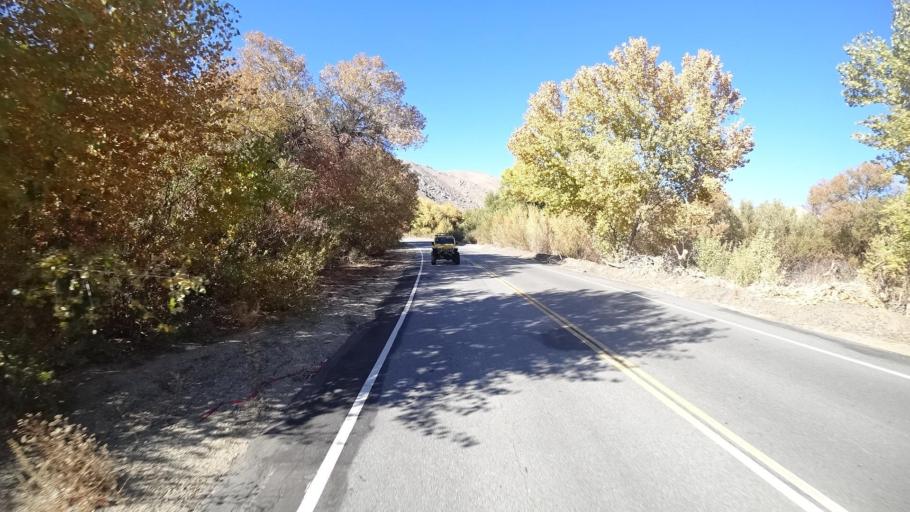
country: US
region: California
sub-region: Kern County
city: Weldon
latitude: 35.6696
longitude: -118.3234
